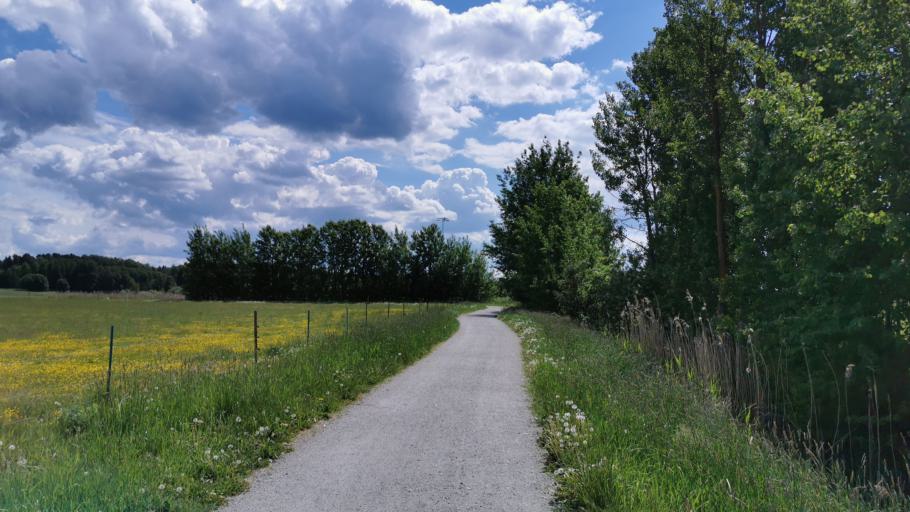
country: SE
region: OErebro
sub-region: Orebro Kommun
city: Orebro
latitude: 59.3007
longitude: 15.2091
